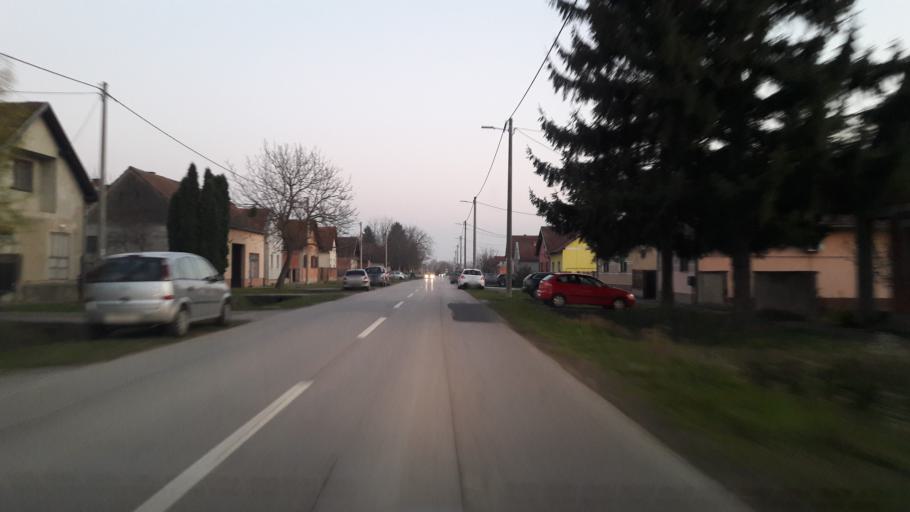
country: HR
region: Vukovarsko-Srijemska
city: Nijemci
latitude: 45.1443
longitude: 19.0348
